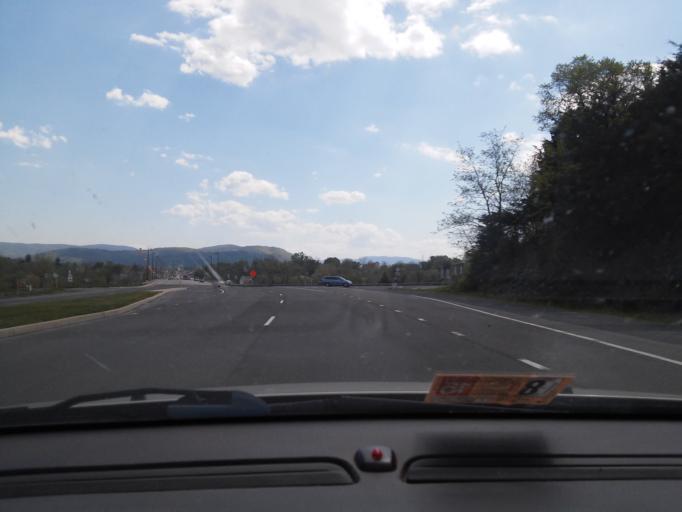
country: US
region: Virginia
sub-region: Warren County
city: Front Royal
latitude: 38.9537
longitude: -78.1998
